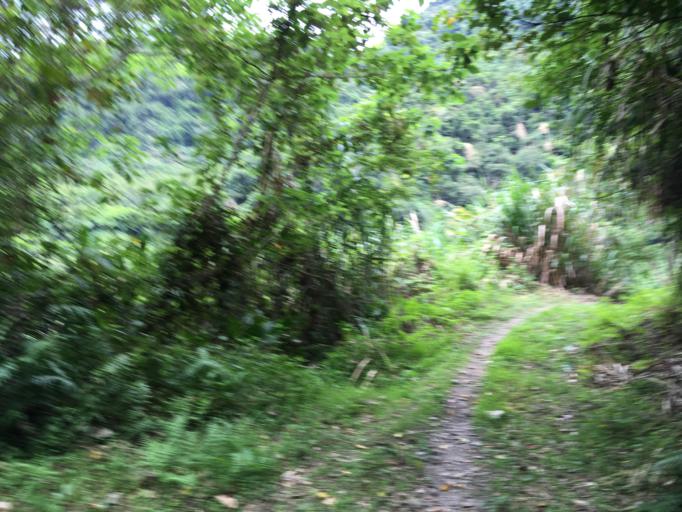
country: TW
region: Taiwan
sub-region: Yilan
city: Yilan
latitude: 24.4236
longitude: 121.7087
